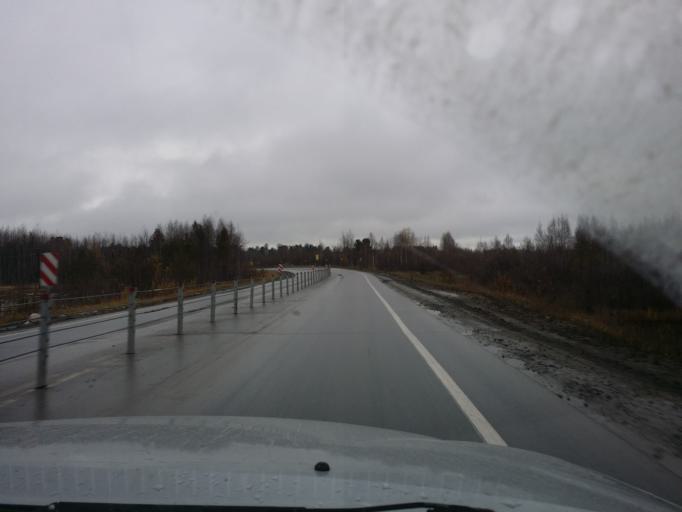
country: RU
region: Khanty-Mansiyskiy Avtonomnyy Okrug
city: Megion
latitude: 61.1093
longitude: 76.0370
